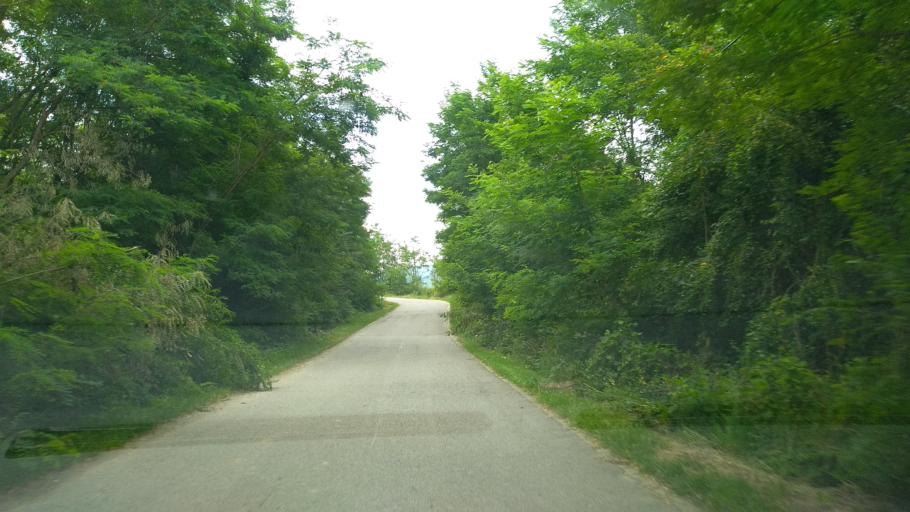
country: RO
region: Hunedoara
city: Salasu de Sus
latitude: 45.5065
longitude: 22.9582
